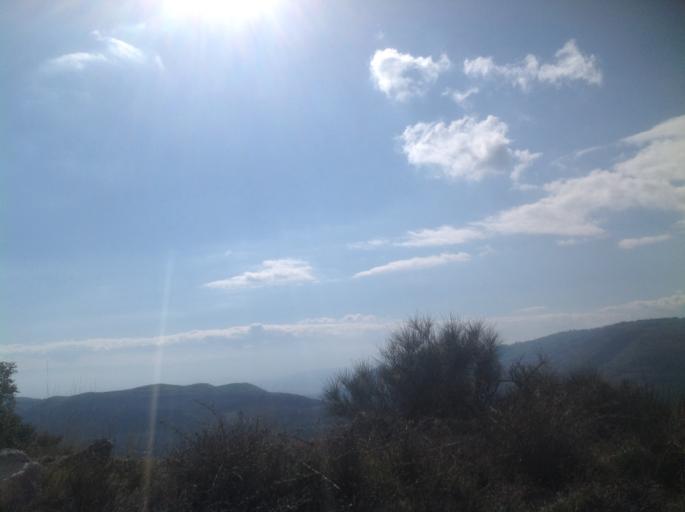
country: IT
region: Calabria
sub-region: Provincia di Cosenza
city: Civita
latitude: 39.8279
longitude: 16.3068
